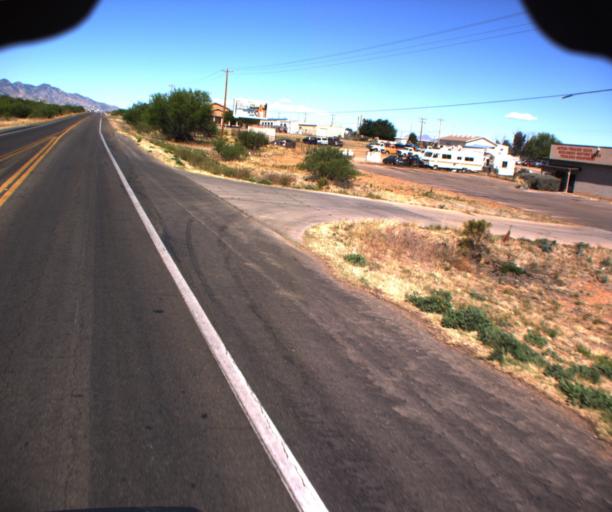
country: US
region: Arizona
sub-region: Cochise County
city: Sierra Vista
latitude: 31.5547
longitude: -110.2087
